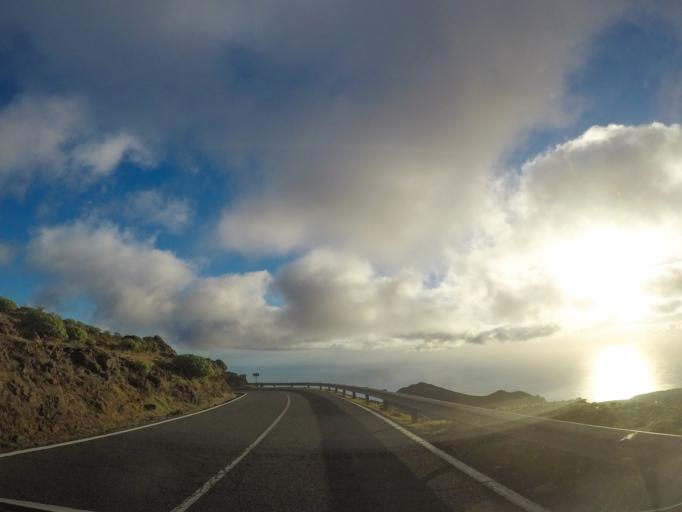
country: ES
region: Canary Islands
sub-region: Provincia de Santa Cruz de Tenerife
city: Alajero
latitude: 28.0873
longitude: -17.2572
